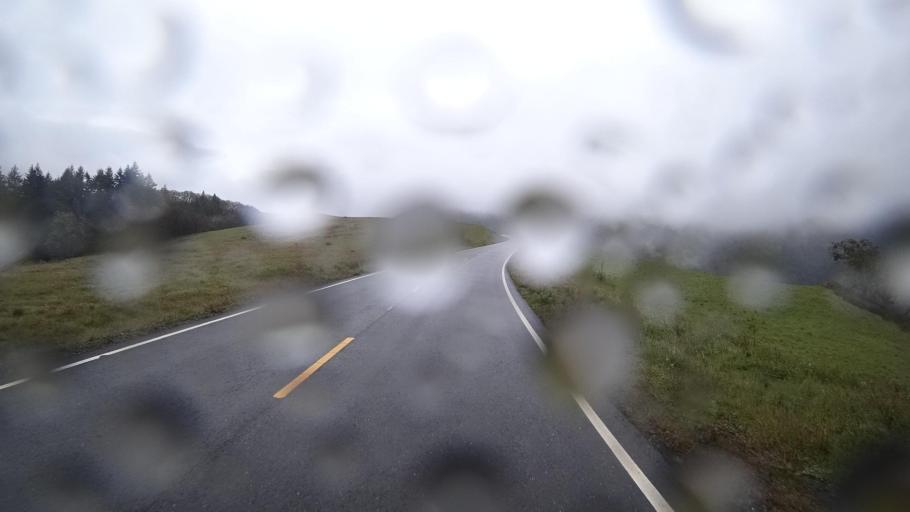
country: US
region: California
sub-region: Humboldt County
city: Westhaven-Moonstone
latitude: 41.1630
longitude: -123.9017
